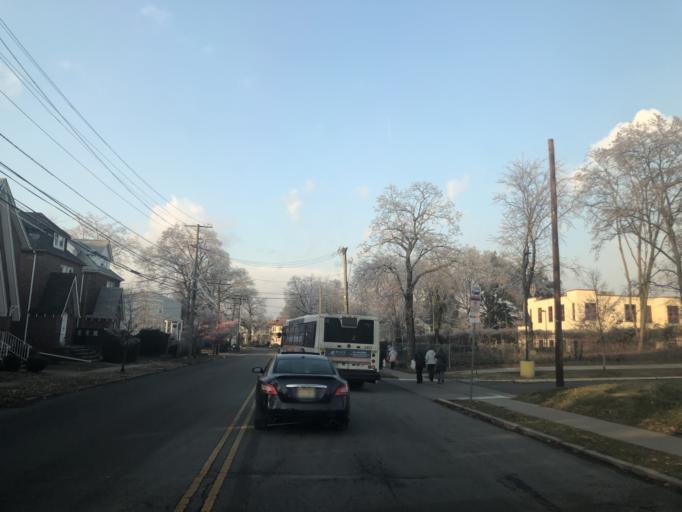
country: US
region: New Jersey
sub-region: Essex County
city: South Orange
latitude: 40.7365
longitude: -74.2511
